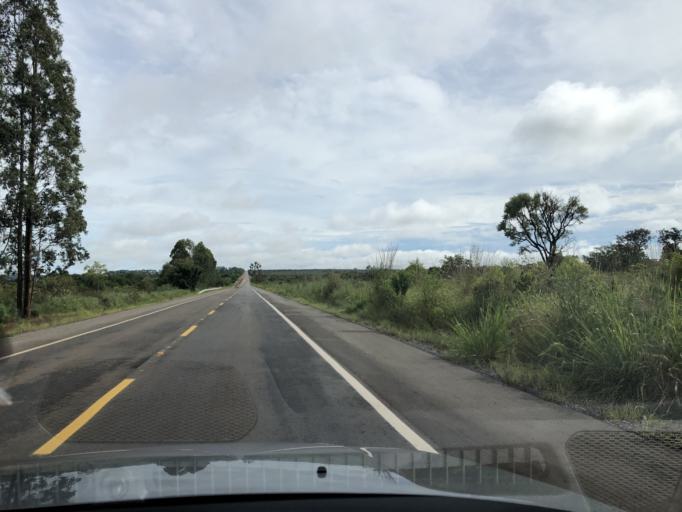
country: BR
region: Federal District
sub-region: Brasilia
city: Brasilia
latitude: -15.6707
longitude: -48.0878
